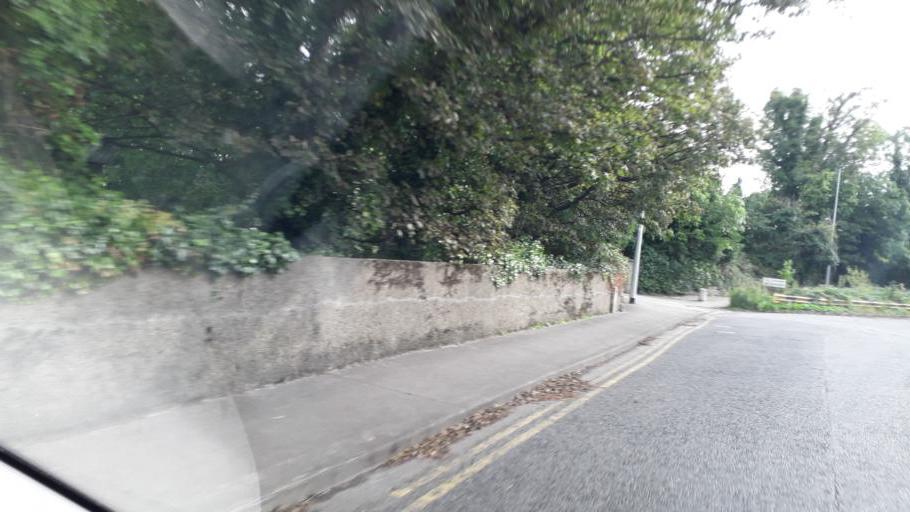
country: IE
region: Leinster
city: Foxrock
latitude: 53.2450
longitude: -6.1992
